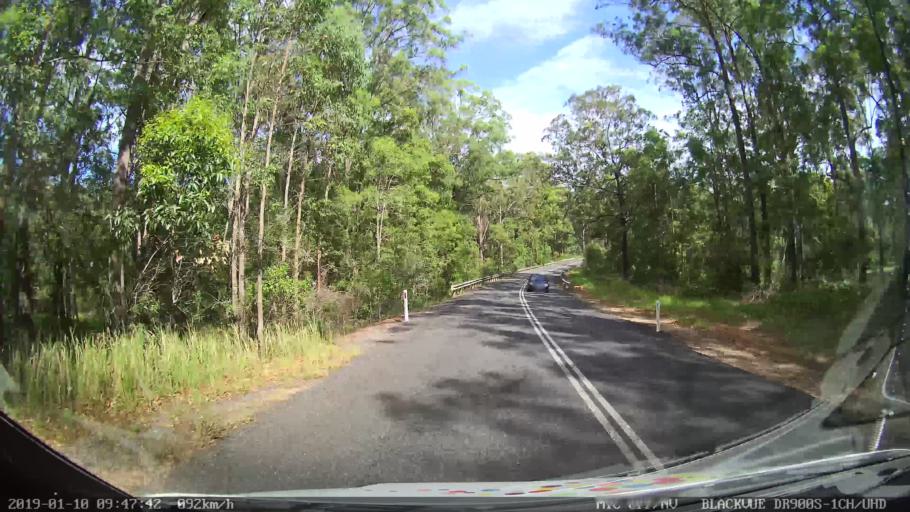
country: AU
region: New South Wales
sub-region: Coffs Harbour
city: Nana Glen
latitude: -30.0817
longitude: 152.9903
